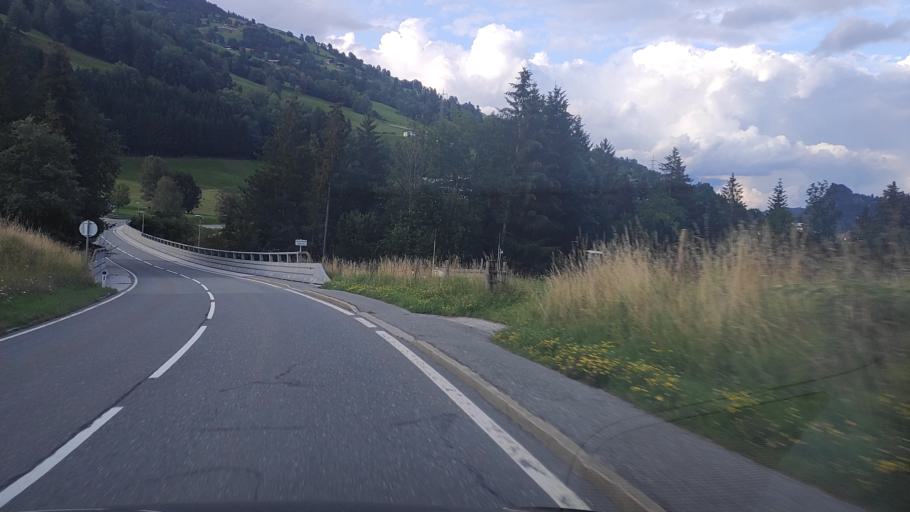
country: AT
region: Salzburg
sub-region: Politischer Bezirk Zell am See
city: Taxenbach
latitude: 47.2909
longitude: 12.9542
